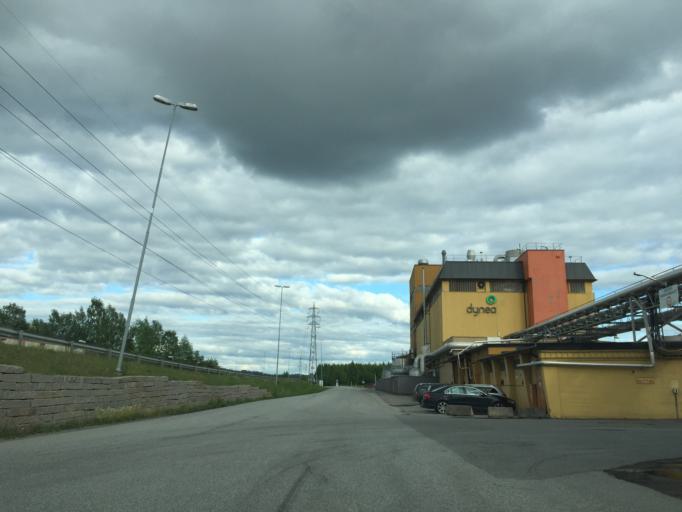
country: NO
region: Akershus
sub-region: Skedsmo
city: Lillestrom
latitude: 59.9476
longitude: 11.0657
